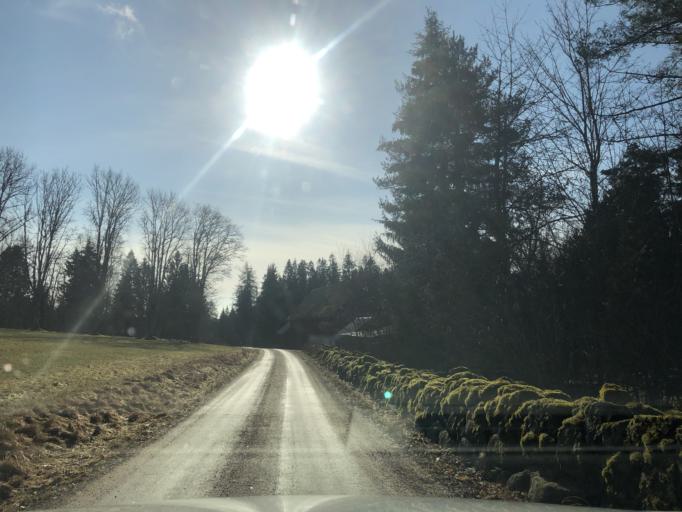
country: SE
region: Vaestra Goetaland
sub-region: Ulricehamns Kommun
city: Ulricehamn
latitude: 57.8098
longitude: 13.3835
